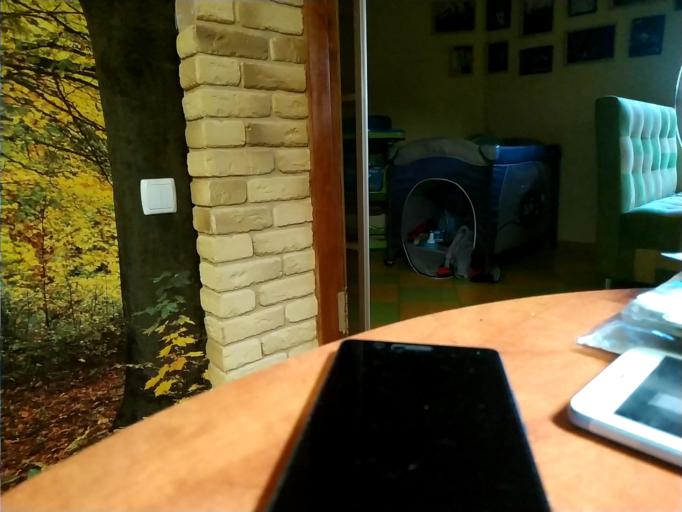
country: RU
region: Orjol
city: Znamenskoye
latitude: 53.4896
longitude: 35.5113
